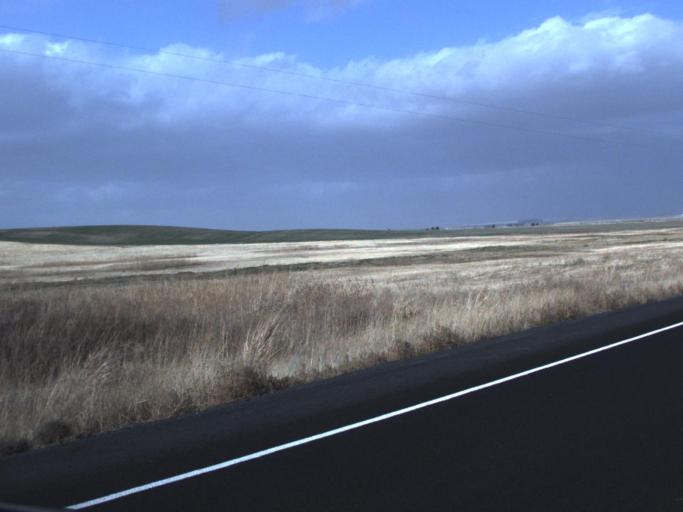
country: US
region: Washington
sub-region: Lincoln County
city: Davenport
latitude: 47.5508
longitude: -118.1848
